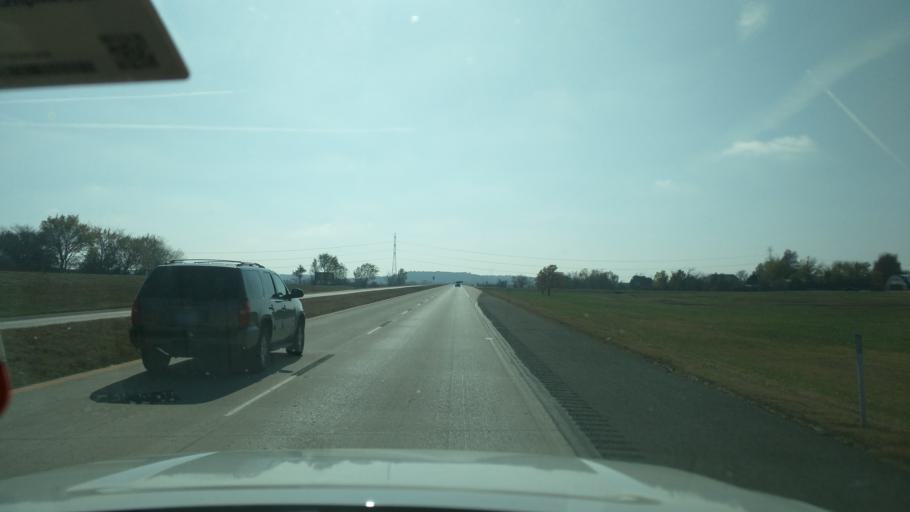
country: US
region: Oklahoma
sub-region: Muskogee County
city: Muskogee
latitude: 35.6963
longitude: -95.3101
